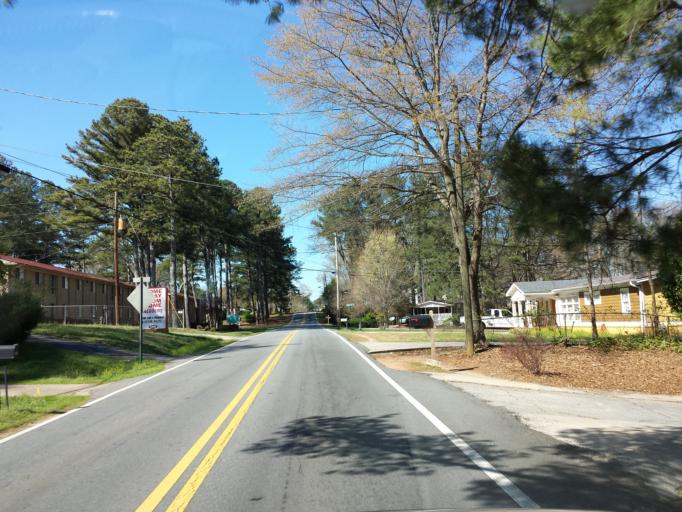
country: US
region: Georgia
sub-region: Cobb County
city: Fair Oaks
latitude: 33.9032
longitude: -84.5533
